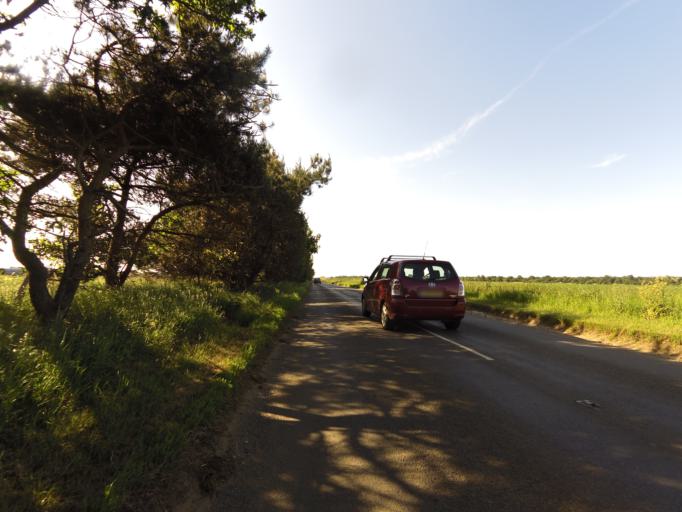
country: GB
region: England
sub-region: Suffolk
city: Woodbridge
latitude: 52.0823
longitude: 1.3603
